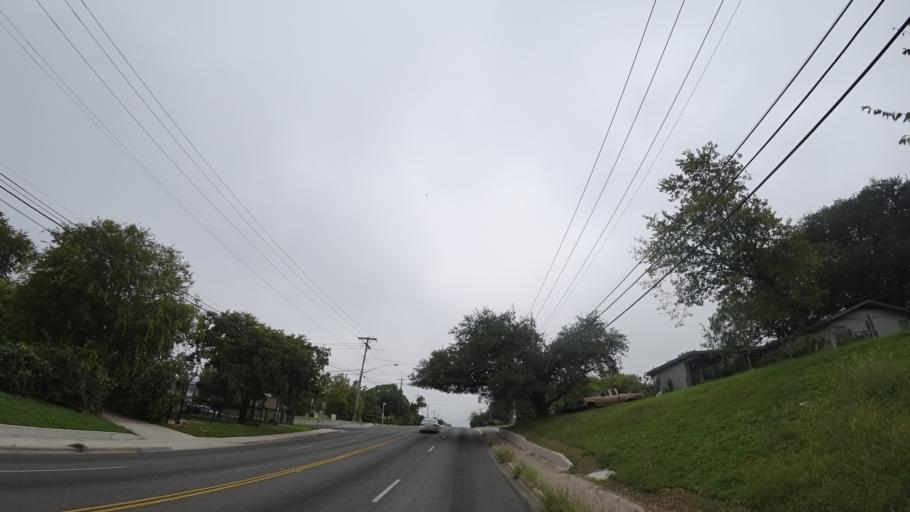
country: US
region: Texas
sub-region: Travis County
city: Austin
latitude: 30.2175
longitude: -97.7750
